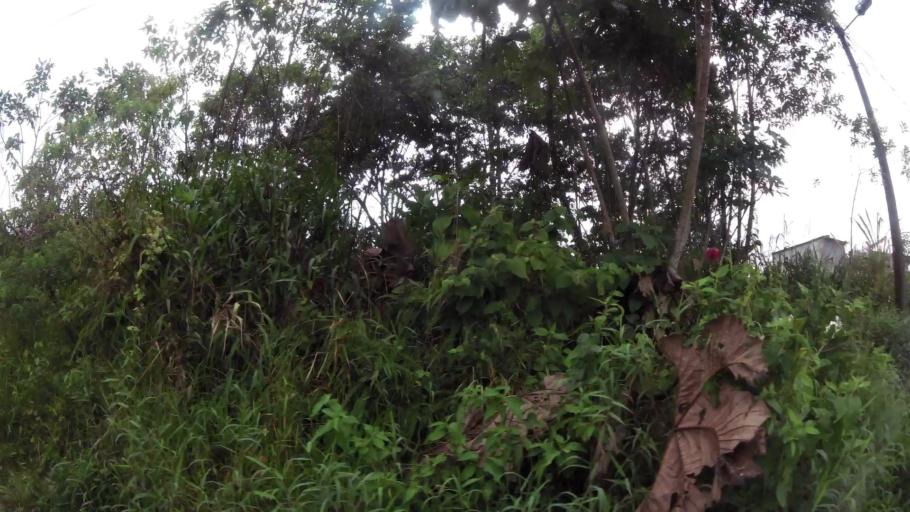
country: EC
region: Pastaza
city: Puyo
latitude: -1.4941
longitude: -77.9909
